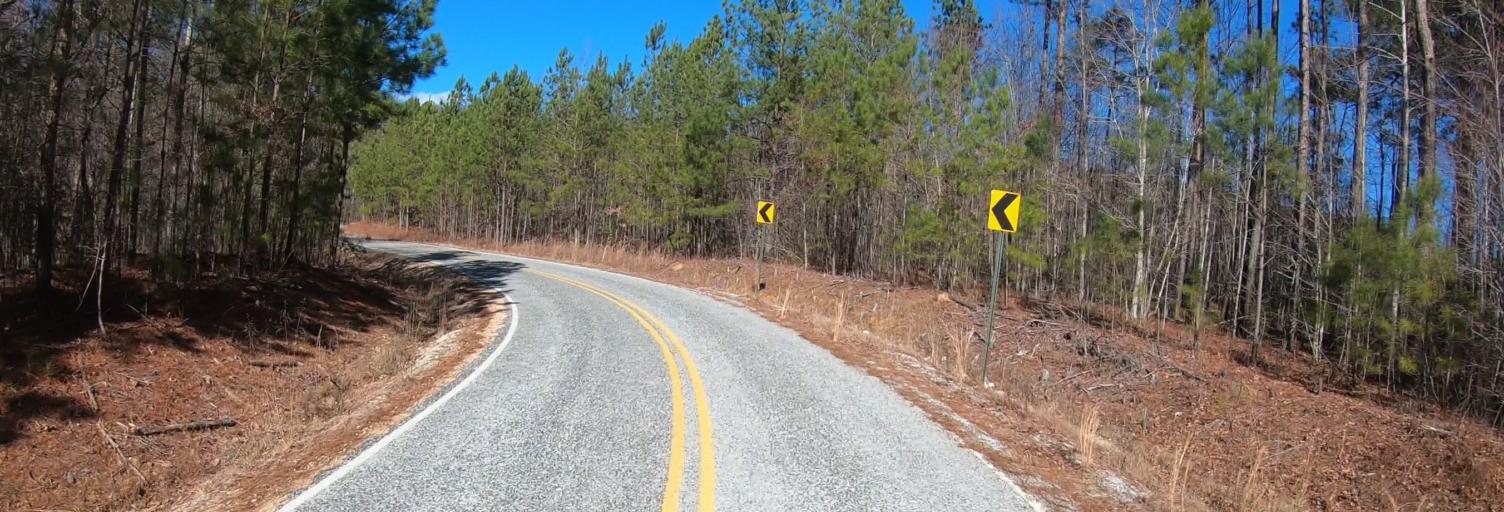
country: US
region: Alabama
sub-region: Clay County
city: Ashland
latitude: 33.3991
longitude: -85.8705
